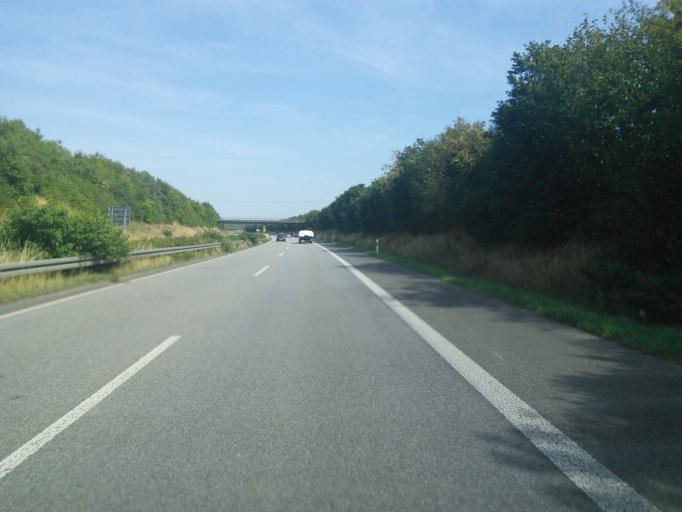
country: DE
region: North Rhine-Westphalia
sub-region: Regierungsbezirk Dusseldorf
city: Bruggen
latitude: 51.2081
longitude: 6.1483
